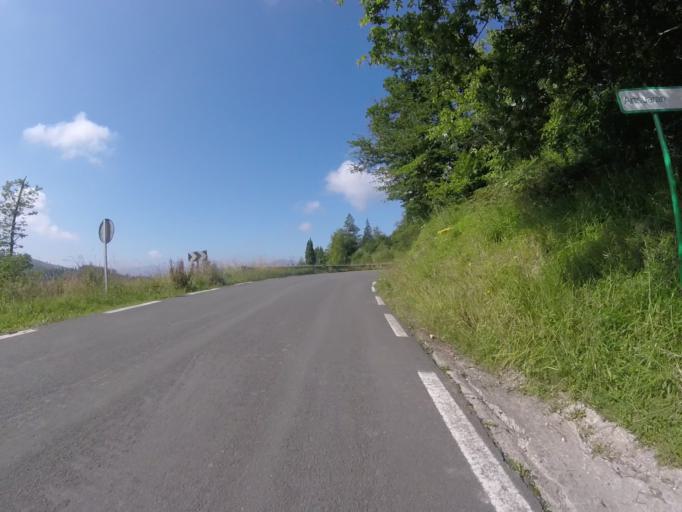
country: ES
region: Basque Country
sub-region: Provincia de Guipuzcoa
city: Ormaiztegui
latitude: 43.0850
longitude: -2.2375
